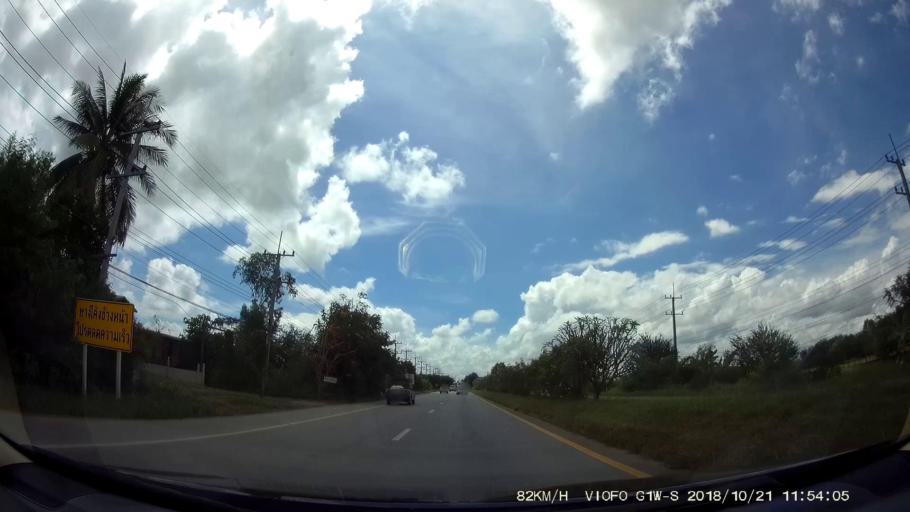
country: TH
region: Chaiyaphum
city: Chatturat
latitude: 15.5884
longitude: 101.9030
